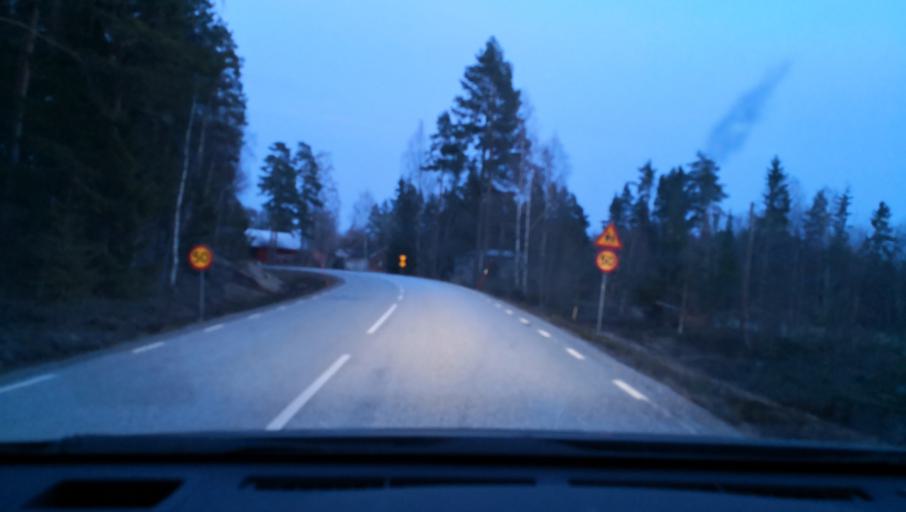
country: SE
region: OErebro
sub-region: Lindesbergs Kommun
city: Frovi
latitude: 59.5860
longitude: 15.4399
